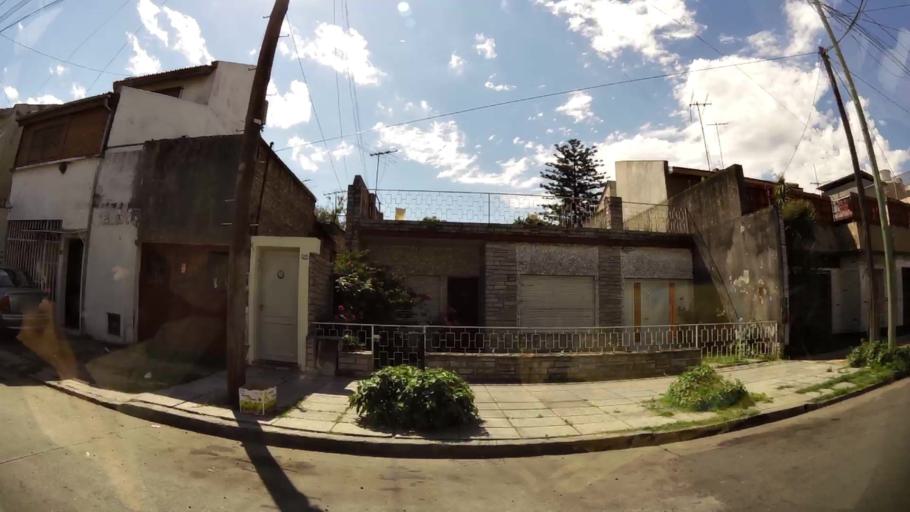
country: AR
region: Buenos Aires
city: San Justo
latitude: -34.6539
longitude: -58.5322
